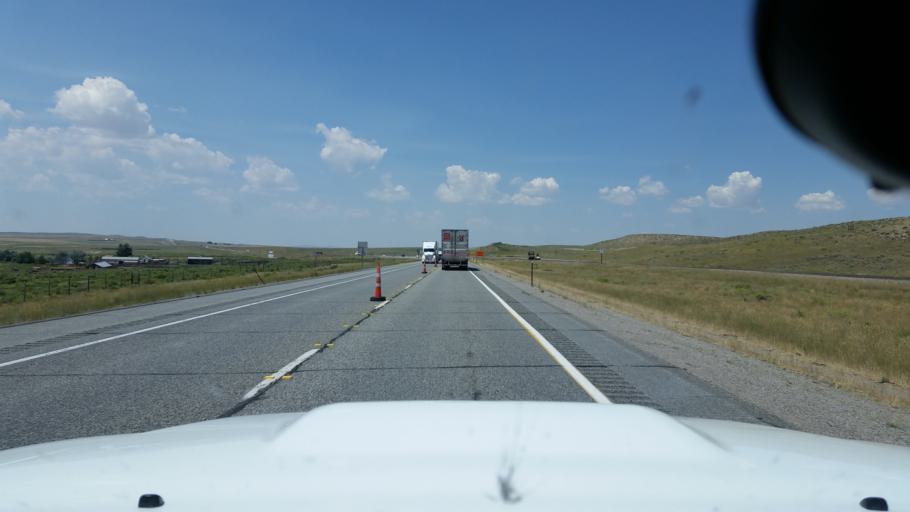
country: US
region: Wyoming
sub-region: Carbon County
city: Saratoga
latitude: 41.7411
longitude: -106.7636
